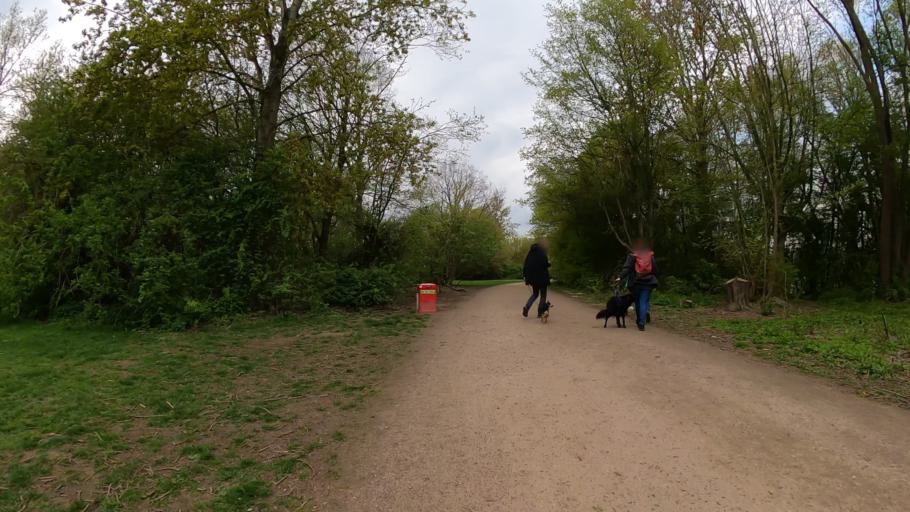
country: DE
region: Hamburg
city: Rothenburgsort
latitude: 53.4847
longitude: 10.0973
